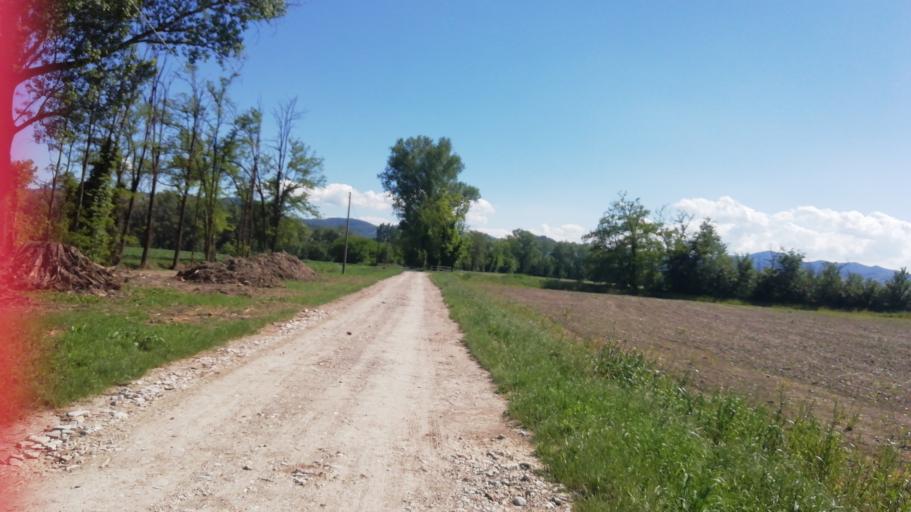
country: IT
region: Emilia-Romagna
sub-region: Provincia di Piacenza
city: Borgonovo Valtidone
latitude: 44.9835
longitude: 9.4590
